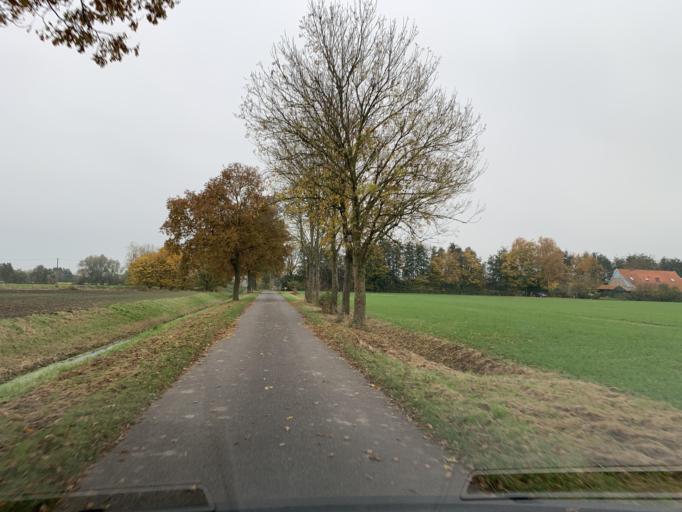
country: DE
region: North Rhine-Westphalia
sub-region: Regierungsbezirk Munster
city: Greven
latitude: 52.0386
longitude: 7.5761
